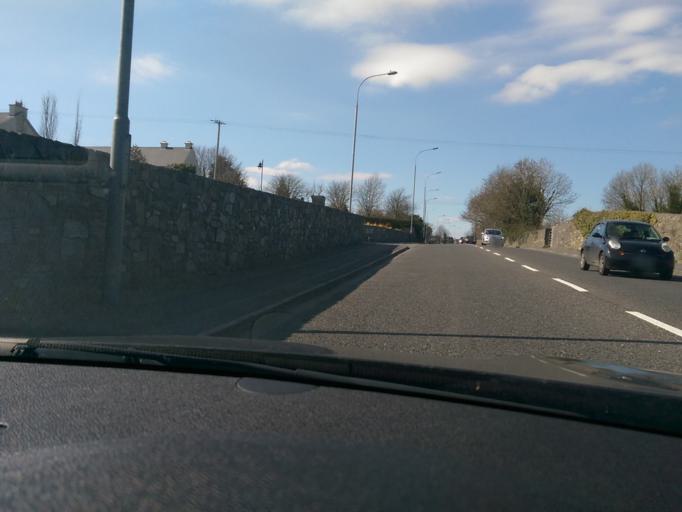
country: IE
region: Connaught
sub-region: County Galway
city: Gaillimh
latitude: 53.2933
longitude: -9.0875
